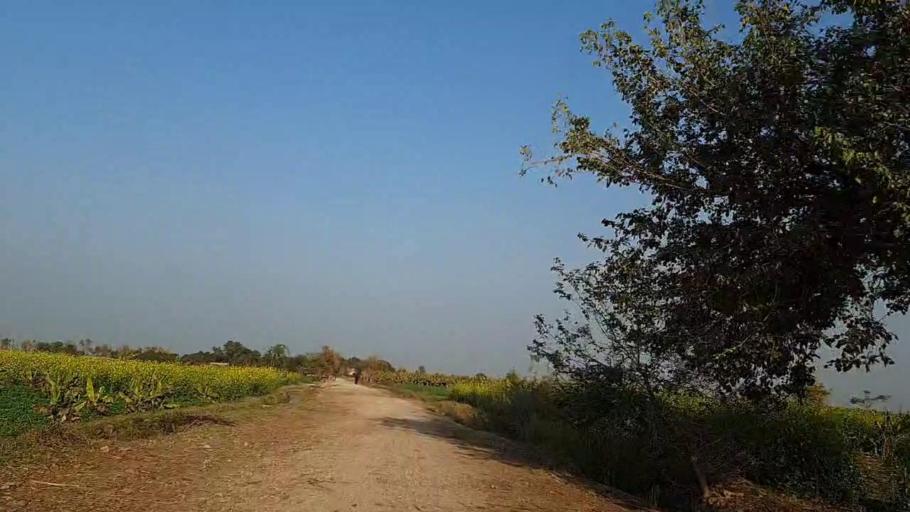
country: PK
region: Sindh
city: Sakrand
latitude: 26.1043
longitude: 68.3673
